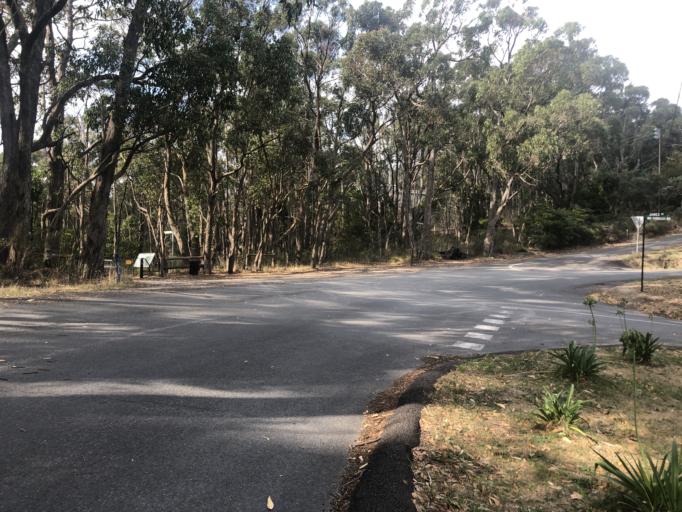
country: AU
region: South Australia
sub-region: Adelaide Hills
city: Crafers
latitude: -34.9945
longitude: 138.7023
